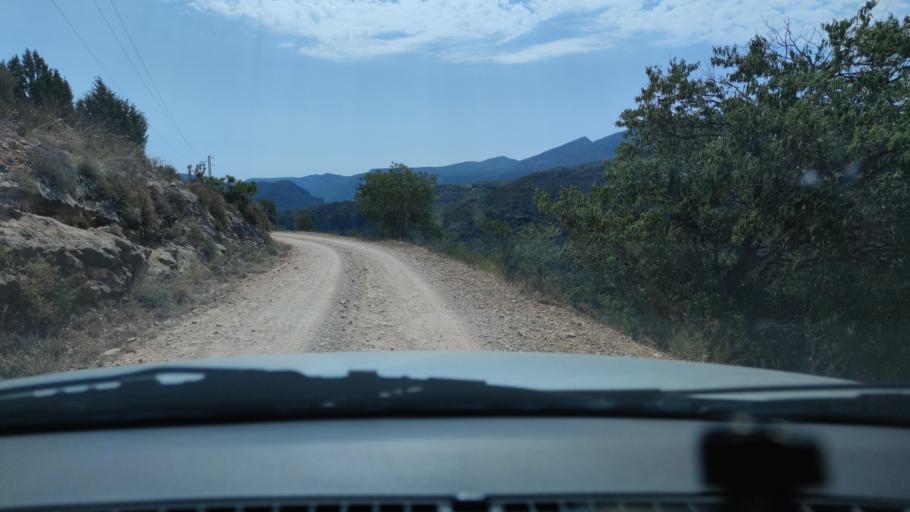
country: ES
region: Catalonia
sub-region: Provincia de Lleida
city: Camarasa
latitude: 41.9274
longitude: 0.8112
